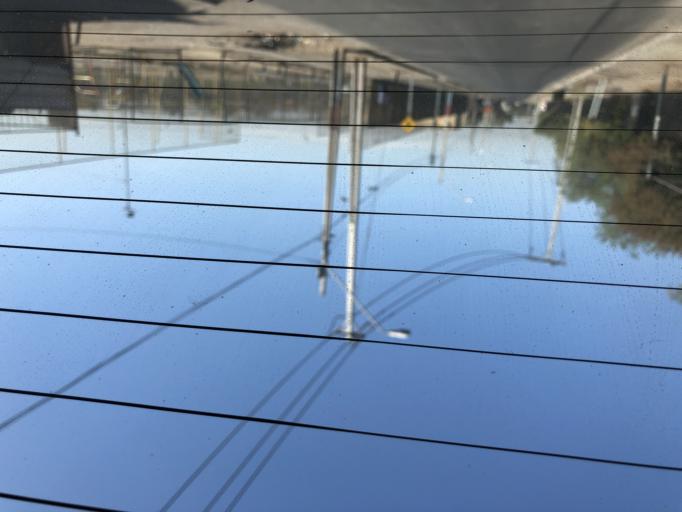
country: CL
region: Santiago Metropolitan
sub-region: Provincia de Santiago
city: La Pintana
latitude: -33.6291
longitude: -70.6223
